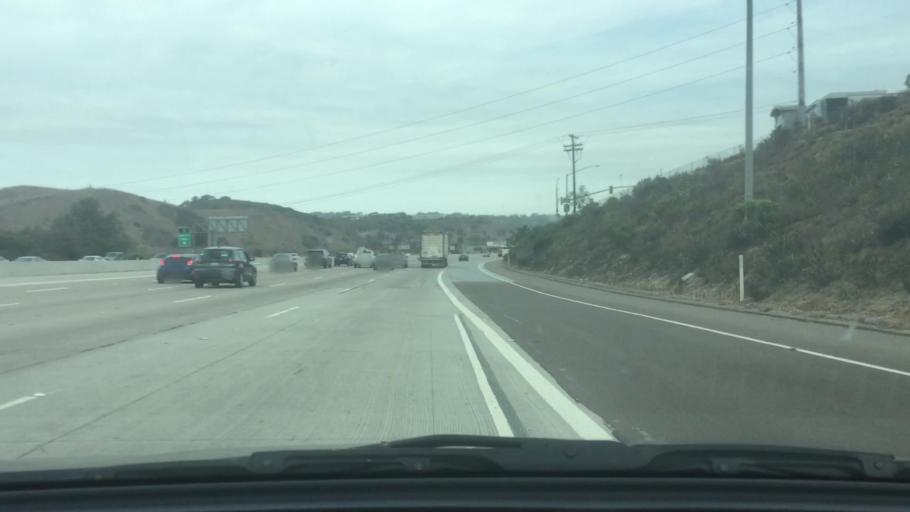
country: US
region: California
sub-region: San Diego County
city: La Jolla
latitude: 32.8932
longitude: -117.2104
